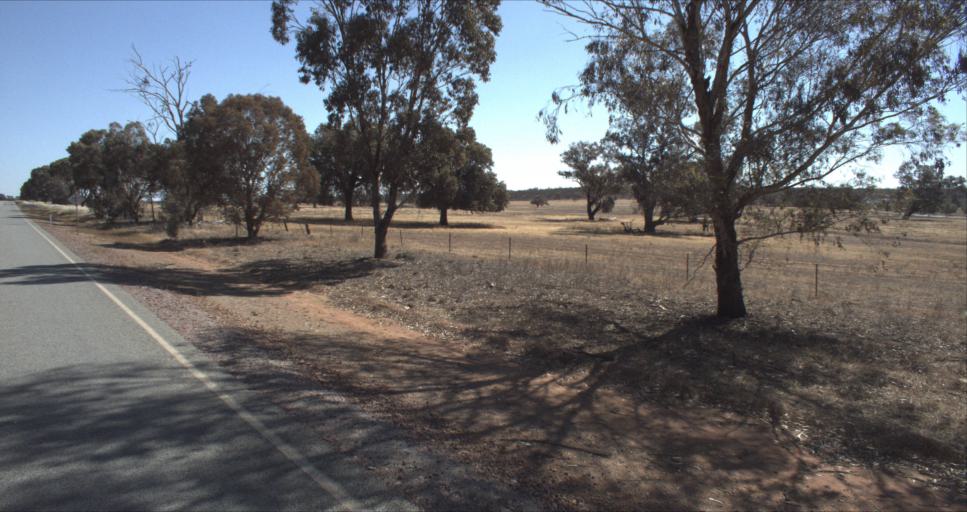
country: AU
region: New South Wales
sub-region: Leeton
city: Leeton
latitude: -34.4810
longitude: 146.4774
